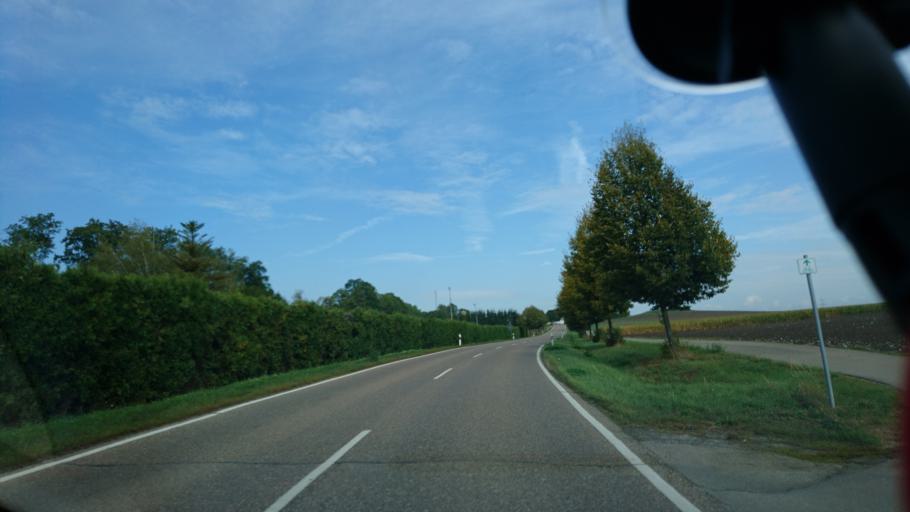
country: DE
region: Baden-Wuerttemberg
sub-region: Regierungsbezirk Stuttgart
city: Vellberg
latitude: 49.1006
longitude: 9.8824
